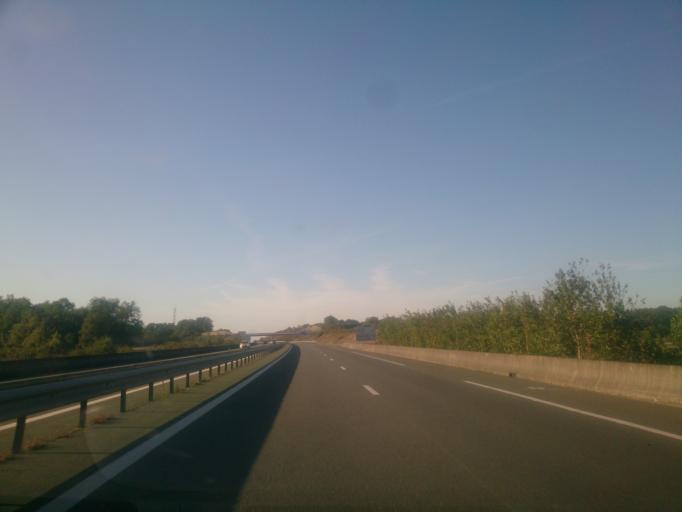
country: FR
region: Midi-Pyrenees
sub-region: Departement du Lot
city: Le Vigan
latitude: 44.7054
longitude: 1.5726
